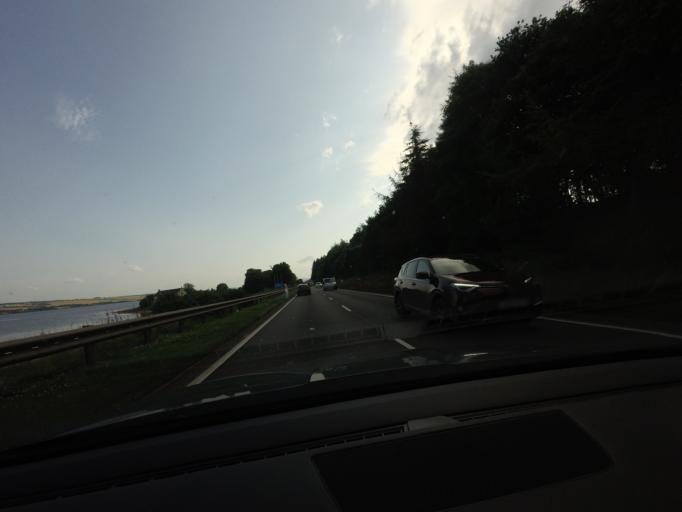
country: GB
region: Scotland
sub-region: Highland
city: Evanton
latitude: 57.6422
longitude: -4.3468
